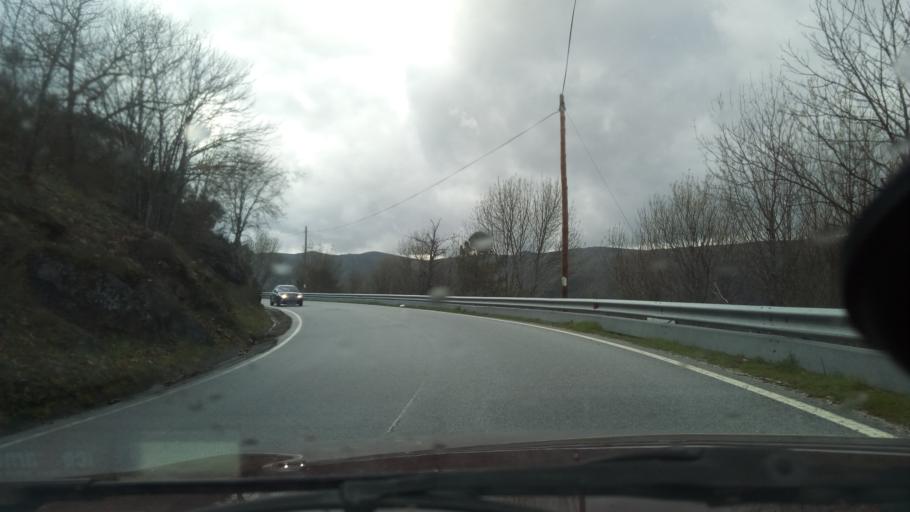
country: PT
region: Guarda
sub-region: Guarda
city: Guarda
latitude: 40.5495
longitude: -7.3200
